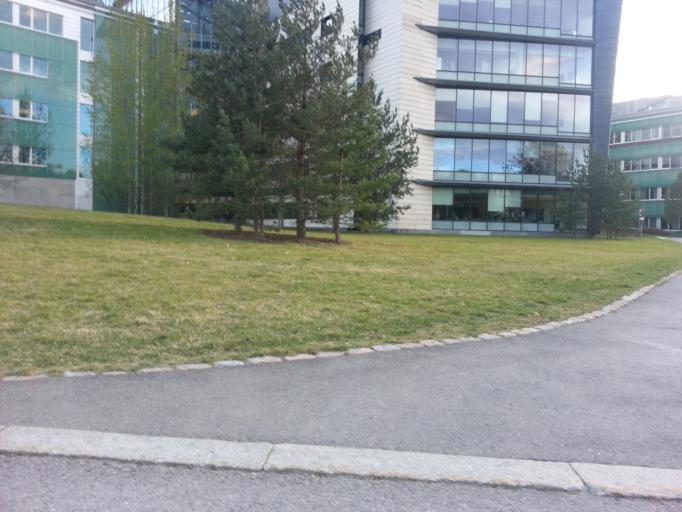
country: NO
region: Akershus
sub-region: Baerum
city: Lysaker
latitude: 59.9011
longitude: 10.6318
